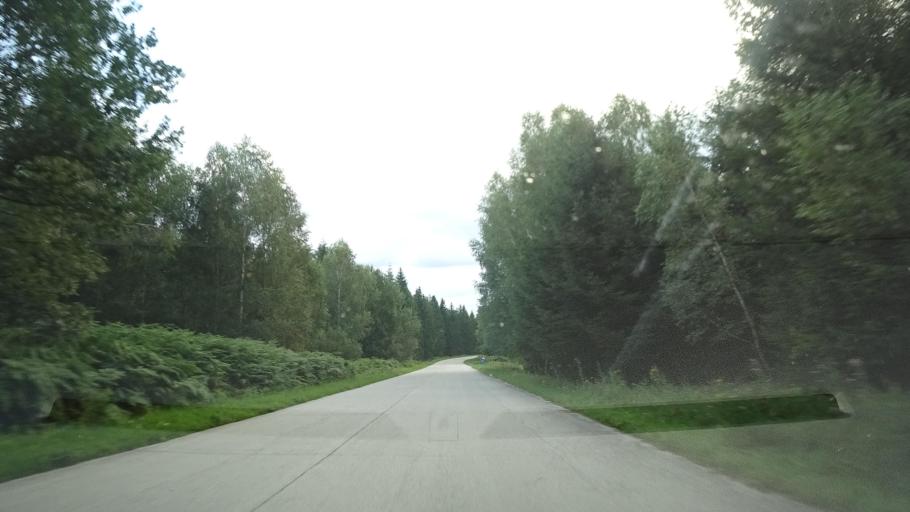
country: BE
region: Wallonia
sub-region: Province du Luxembourg
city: Herbeumont
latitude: 49.8009
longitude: 5.2597
